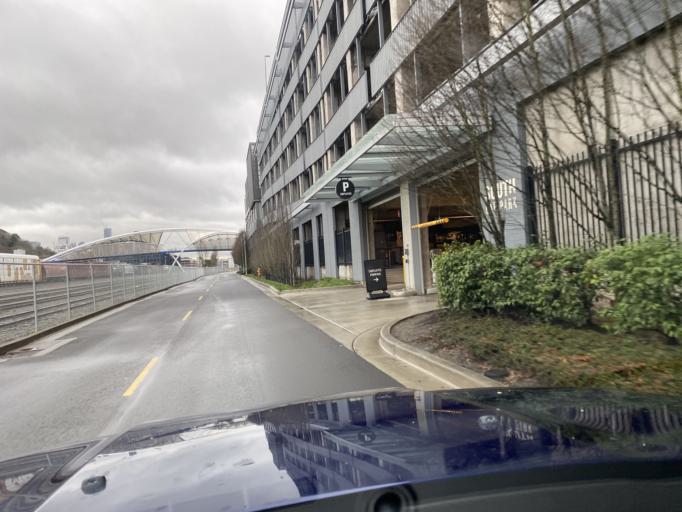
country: US
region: Washington
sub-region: King County
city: Seattle
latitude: 47.6295
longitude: -122.3743
